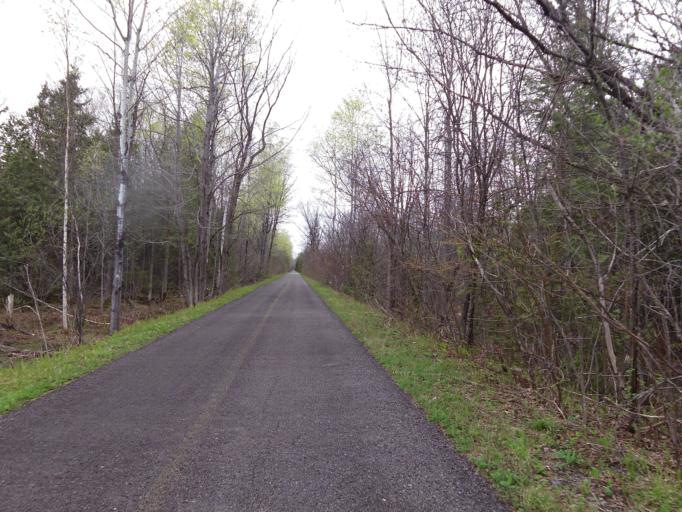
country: CA
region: Quebec
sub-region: Laurentides
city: Lachute
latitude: 45.5794
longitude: -74.3935
